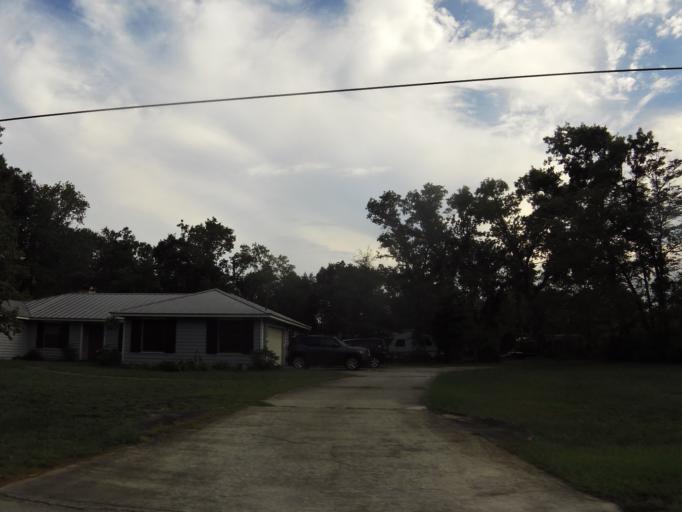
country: US
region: Florida
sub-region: Saint Johns County
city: Fruit Cove
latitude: 30.0953
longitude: -81.6269
